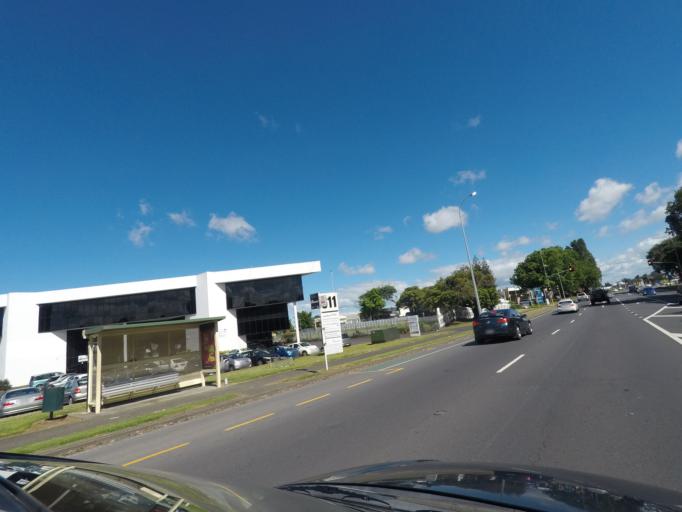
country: NZ
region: Auckland
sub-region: Auckland
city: Manukau City
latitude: -36.9859
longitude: 174.8805
